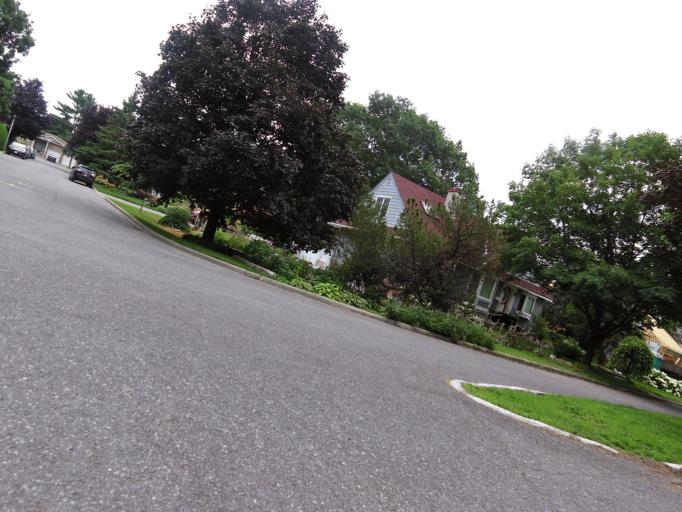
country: CA
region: Ontario
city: Ottawa
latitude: 45.3671
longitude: -75.7632
